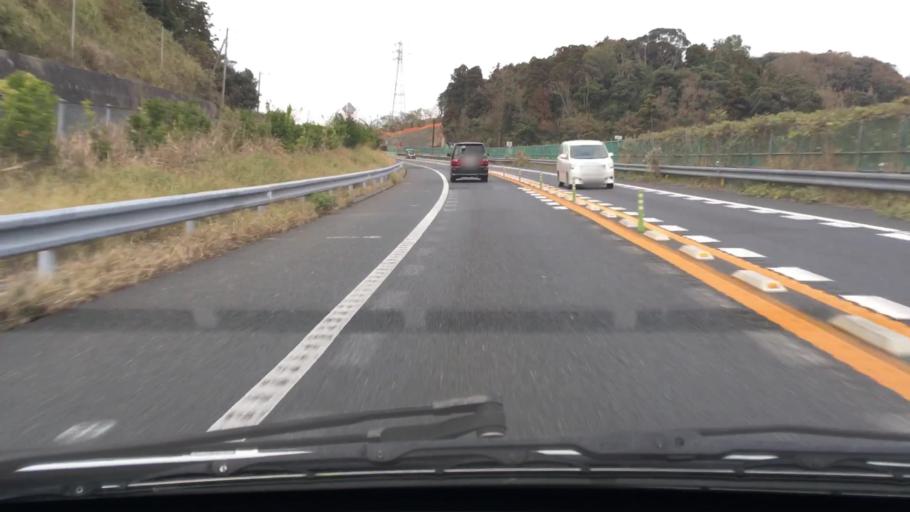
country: JP
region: Chiba
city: Kimitsu
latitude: 35.2276
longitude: 139.8866
